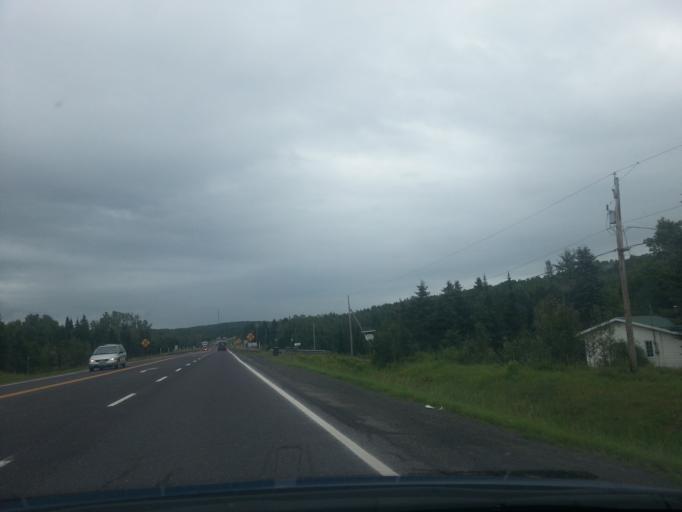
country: CA
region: Quebec
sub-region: Bas-Saint-Laurent
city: Pohenegamook
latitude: 47.6835
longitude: -69.2274
